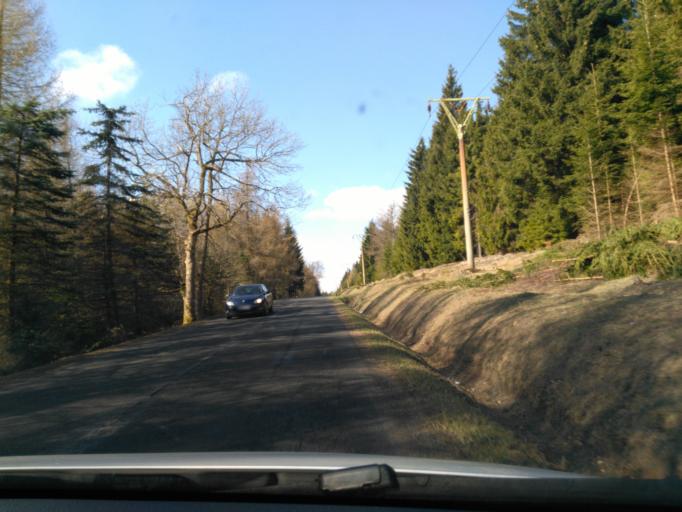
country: CZ
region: Ustecky
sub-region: Okres Chomutov
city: Kovarska
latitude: 50.4588
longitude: 13.0913
